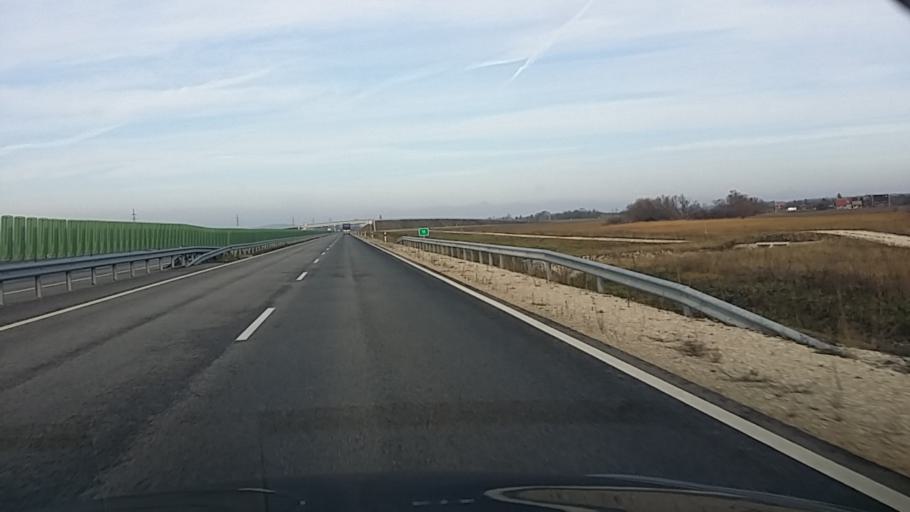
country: HU
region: Fejer
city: Sarszentmihaly
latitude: 47.1960
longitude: 18.3491
